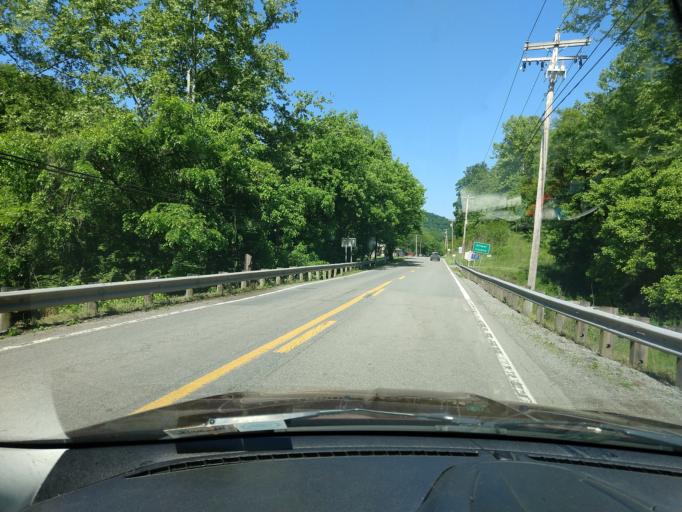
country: US
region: West Virginia
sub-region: Gilmer County
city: Glenville
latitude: 38.8766
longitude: -80.7039
